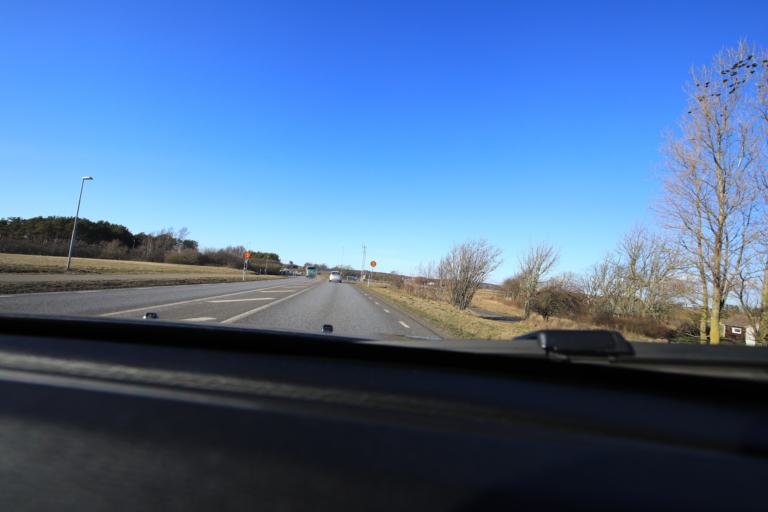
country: SE
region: Halland
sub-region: Varbergs Kommun
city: Traslovslage
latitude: 57.0707
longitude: 12.2898
